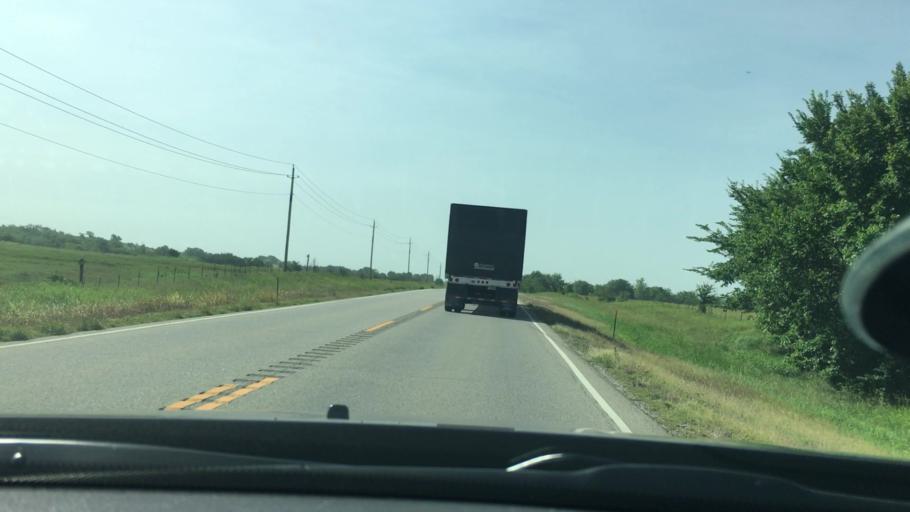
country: US
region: Oklahoma
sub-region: Atoka County
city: Atoka
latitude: 34.4413
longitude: -96.2043
